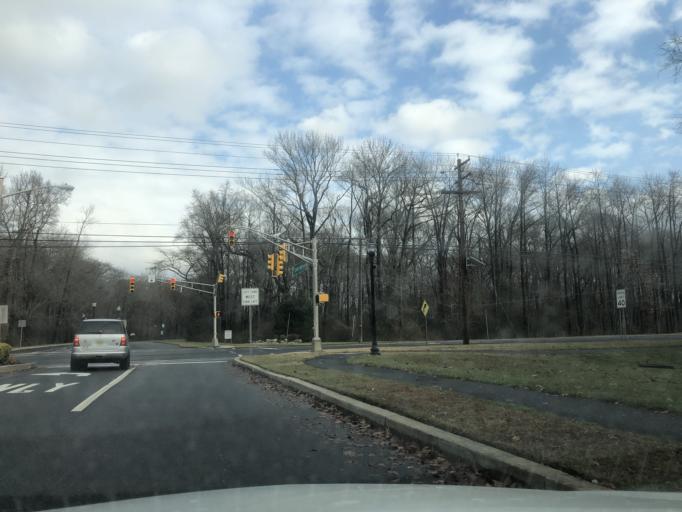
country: US
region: New Jersey
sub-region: Camden County
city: Bellmawr
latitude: 39.8439
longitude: -75.1041
